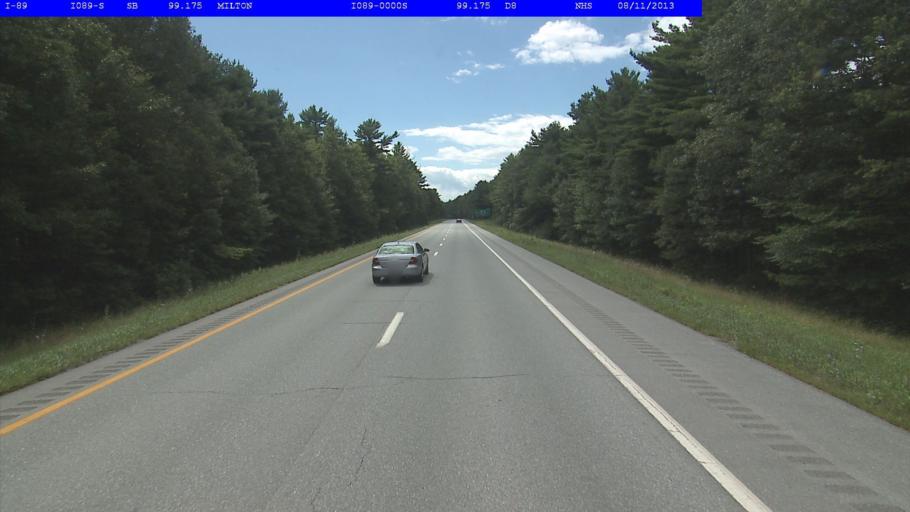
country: US
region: Vermont
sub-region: Chittenden County
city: Milton
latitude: 44.6080
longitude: -73.1684
